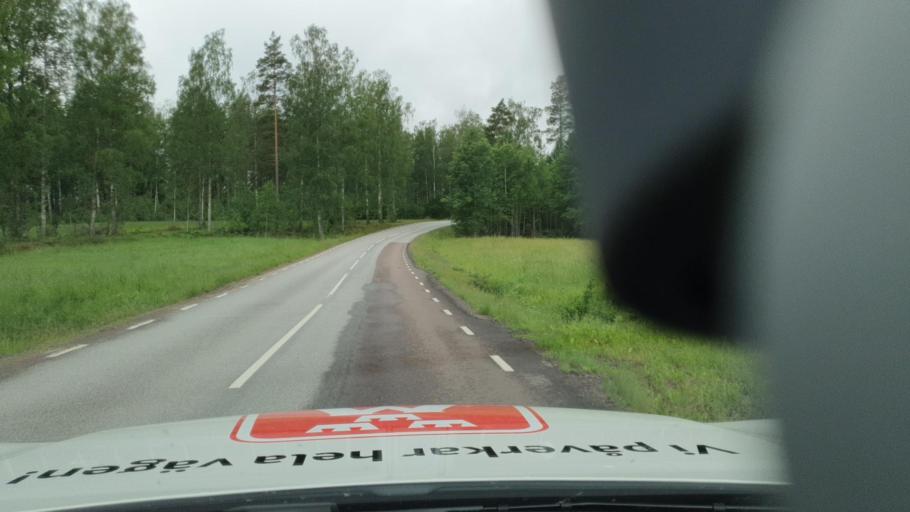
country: SE
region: Vaermland
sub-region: Kristinehamns Kommun
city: Bjorneborg
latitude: 59.1030
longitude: 14.2446
